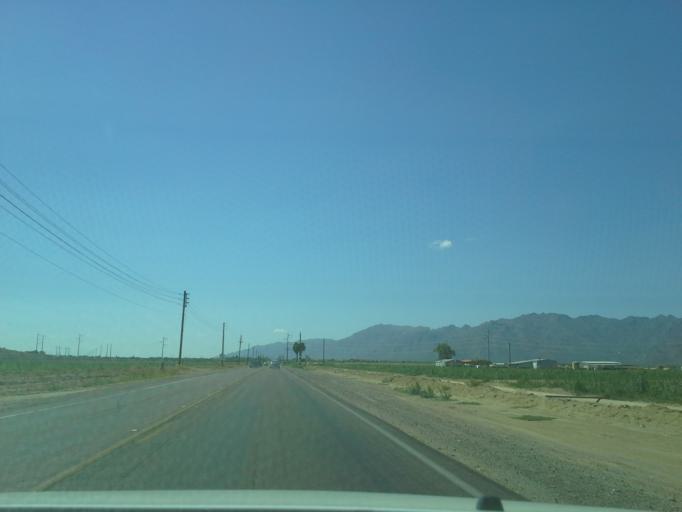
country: US
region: Arizona
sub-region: Maricopa County
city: Laveen
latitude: 33.3338
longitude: -112.1692
